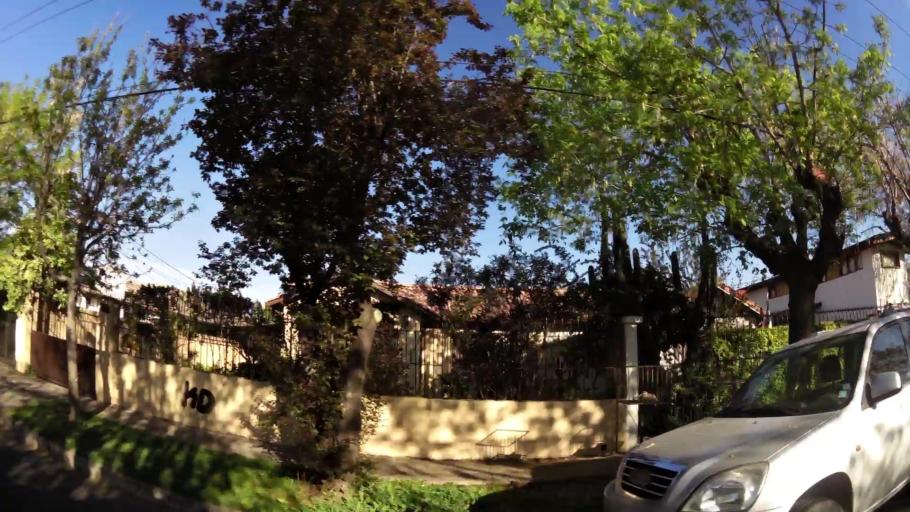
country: CL
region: Santiago Metropolitan
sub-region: Provincia de Santiago
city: Villa Presidente Frei, Nunoa, Santiago, Chile
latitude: -33.4599
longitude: -70.5650
